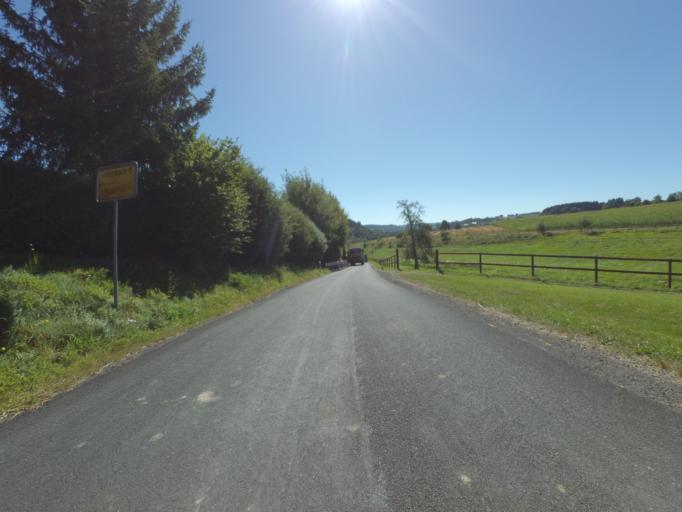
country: DE
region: Rheinland-Pfalz
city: Utzerath
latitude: 50.2223
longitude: 6.9382
